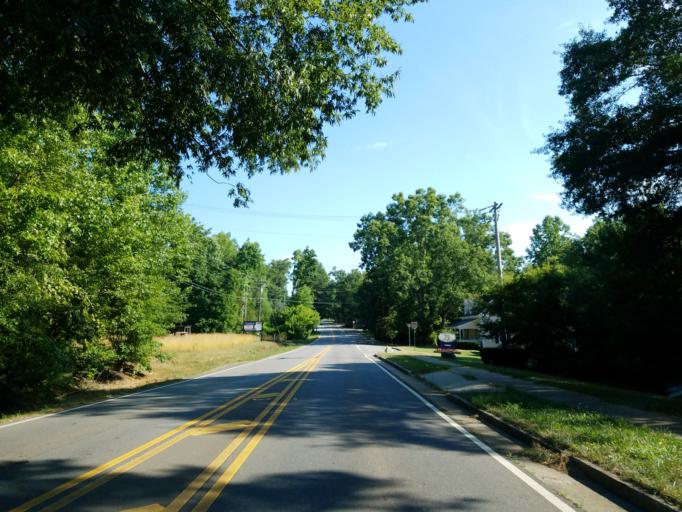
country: US
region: Georgia
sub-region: Fulton County
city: Milton
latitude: 34.1645
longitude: -84.3336
